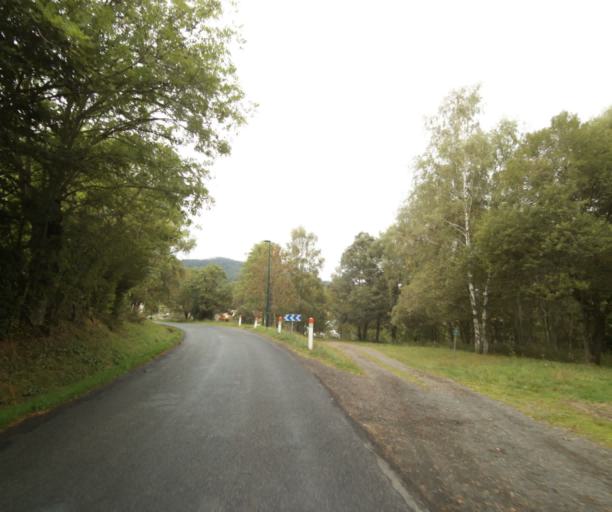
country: FR
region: Auvergne
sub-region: Departement du Puy-de-Dome
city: Saint-Genes-Champanelle
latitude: 45.7396
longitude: 2.9688
